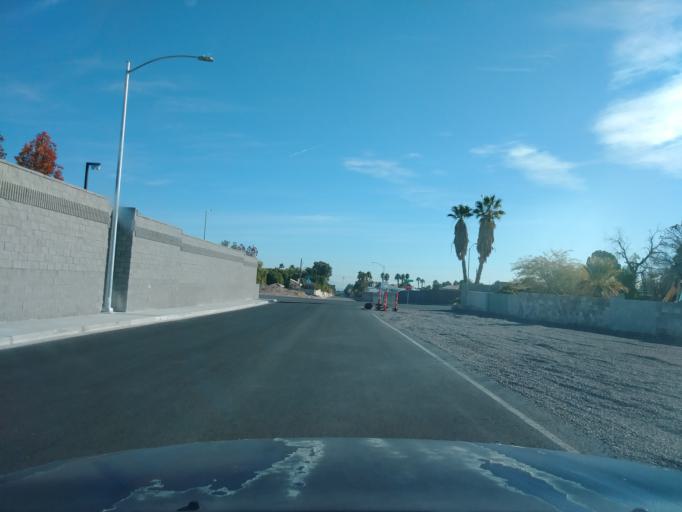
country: US
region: Nevada
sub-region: Clark County
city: Spring Valley
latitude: 36.1496
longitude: -115.2713
